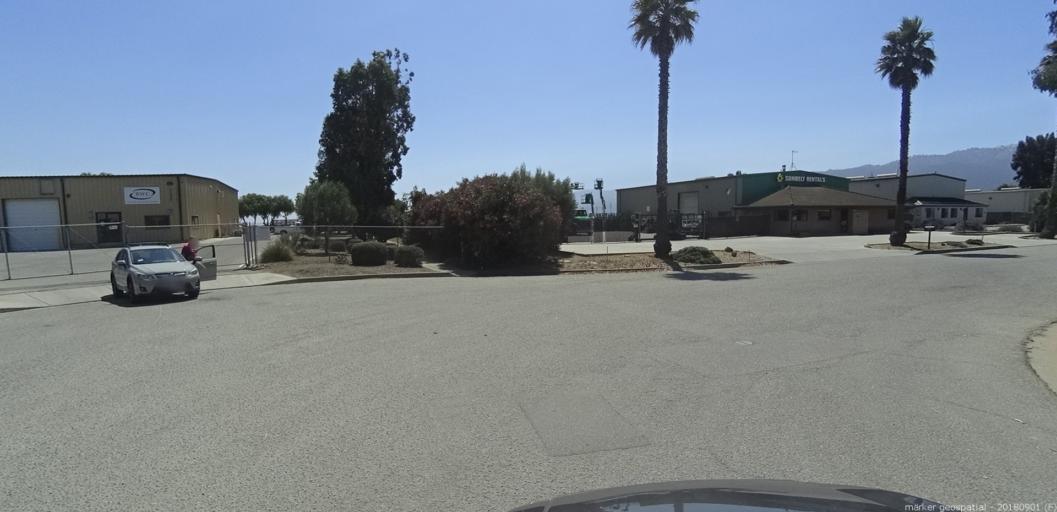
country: US
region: California
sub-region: Monterey County
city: Chualar
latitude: 36.6057
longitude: -121.5541
